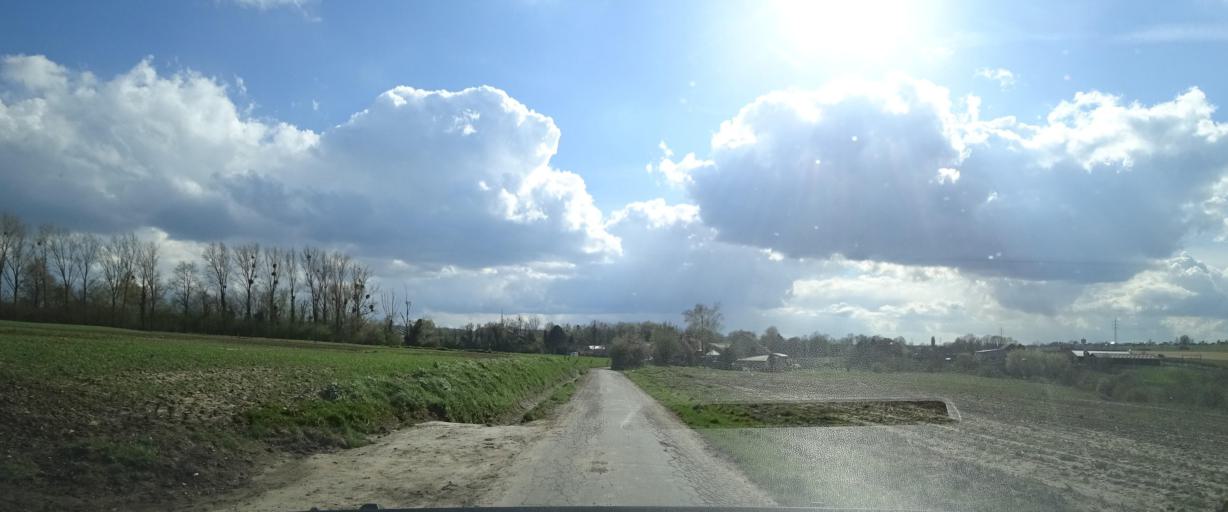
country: BE
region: Wallonia
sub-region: Province du Brabant Wallon
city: Tubize
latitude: 50.6557
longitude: 4.1846
